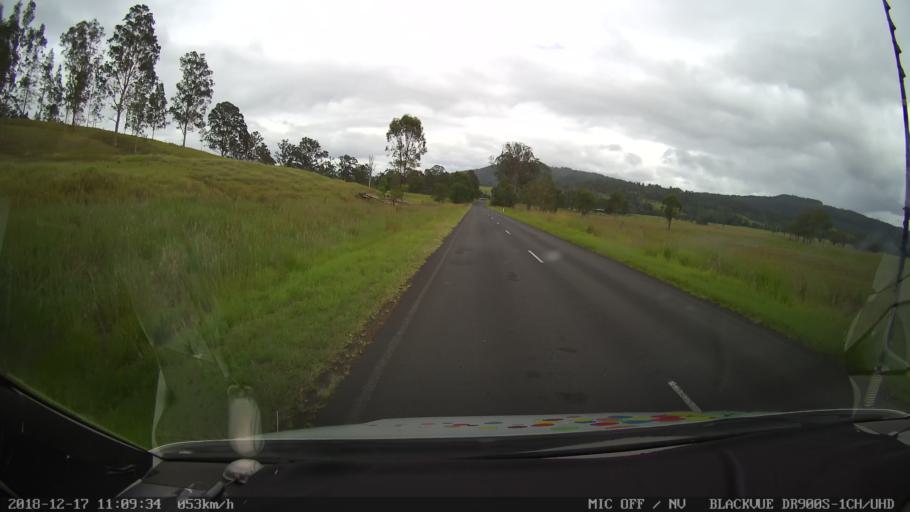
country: AU
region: New South Wales
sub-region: Kyogle
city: Kyogle
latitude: -28.7535
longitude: 152.6537
